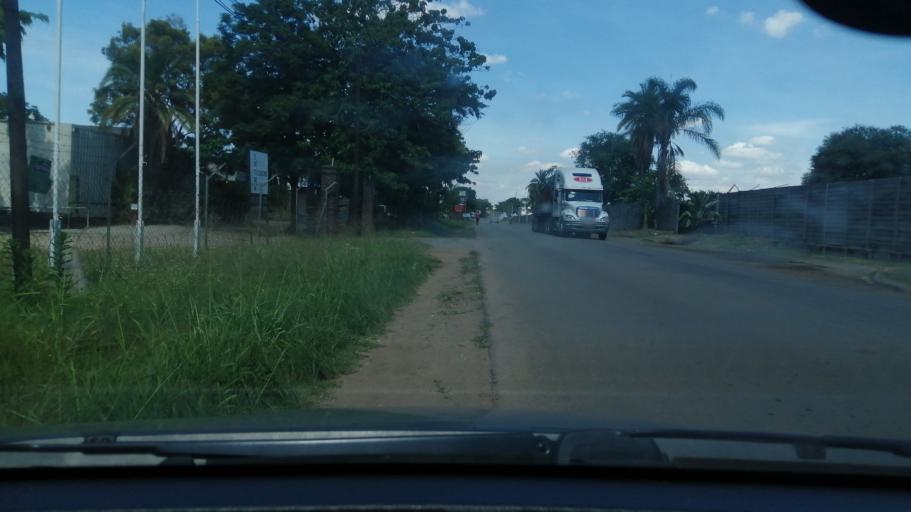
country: ZW
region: Harare
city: Epworth
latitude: -17.8447
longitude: 31.1178
